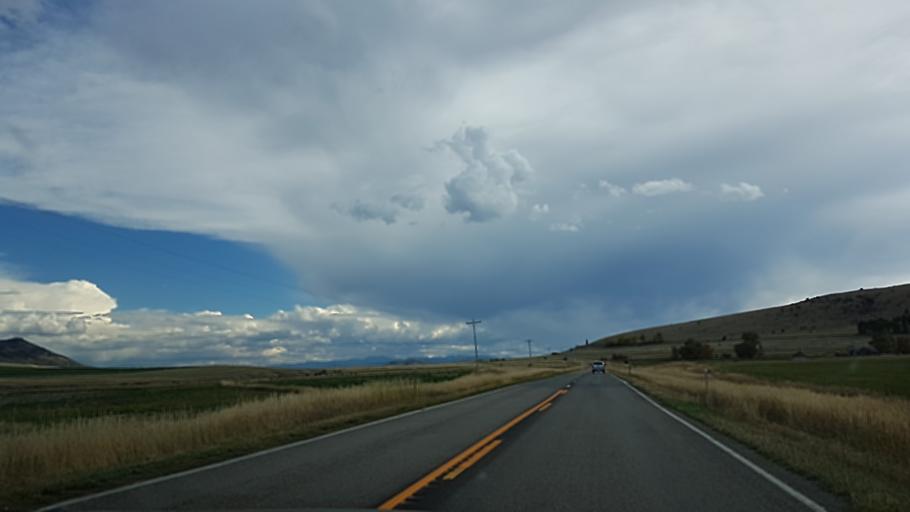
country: US
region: Montana
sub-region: Jefferson County
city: Whitehall
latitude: 45.7835
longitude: -111.9152
